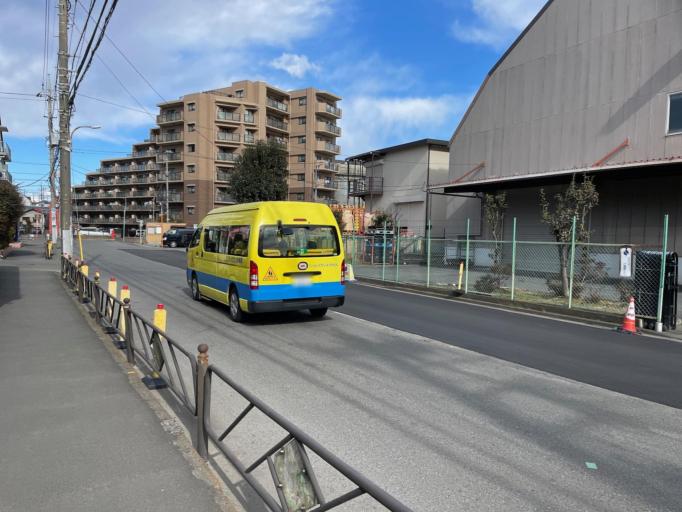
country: JP
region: Tokyo
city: Chofugaoka
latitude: 35.6490
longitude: 139.5305
